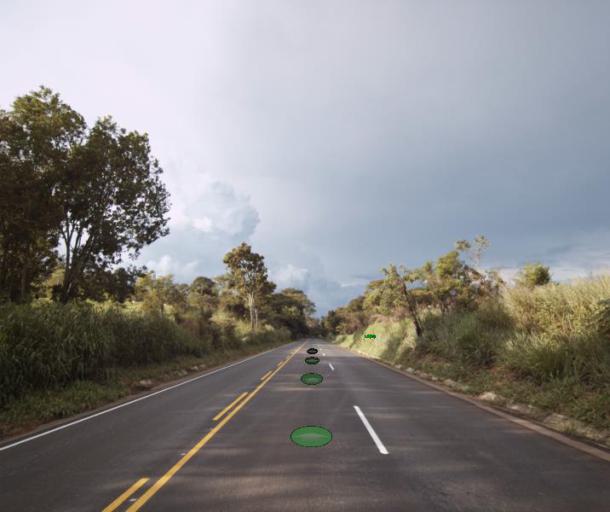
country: BR
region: Goias
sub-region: Ceres
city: Ceres
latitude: -15.1537
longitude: -49.5372
